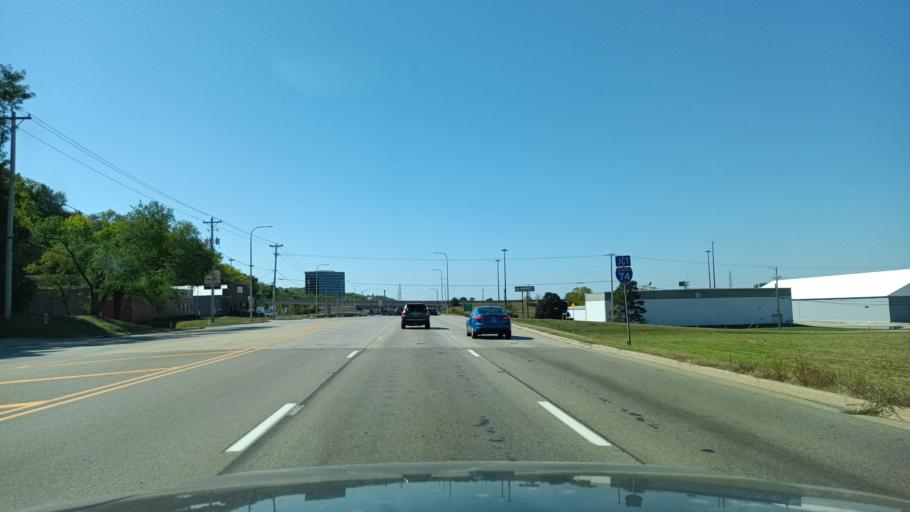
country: US
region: Illinois
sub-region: Tazewell County
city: East Peoria
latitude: 40.6726
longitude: -89.5698
